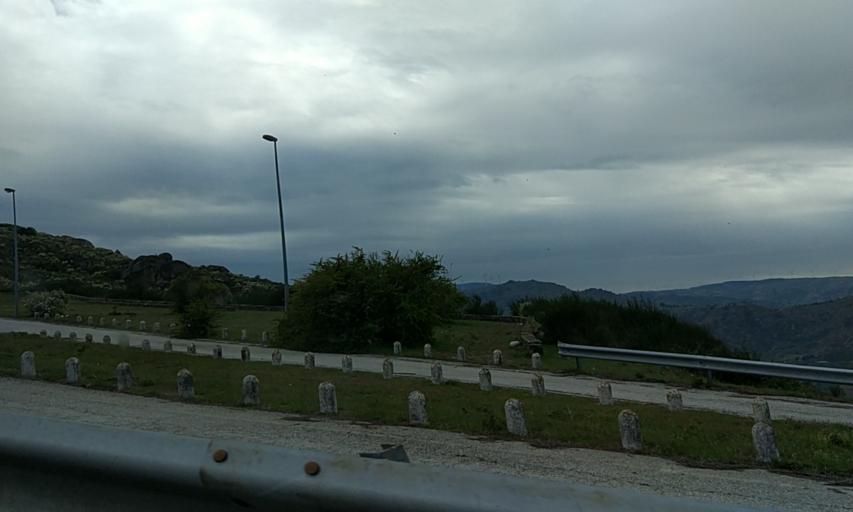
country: PT
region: Guarda
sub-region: Guarda
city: Guarda
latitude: 40.5905
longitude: -7.2746
